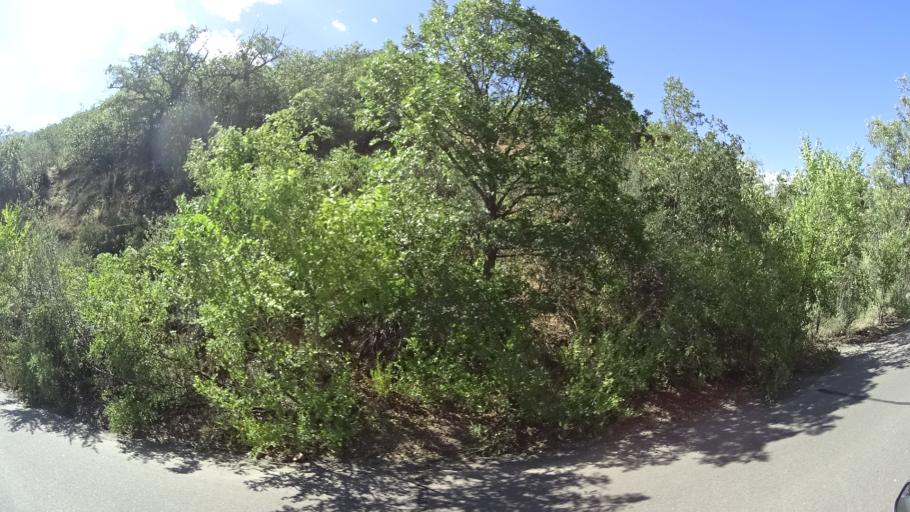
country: US
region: Colorado
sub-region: El Paso County
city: Manitou Springs
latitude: 38.8294
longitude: -104.8800
